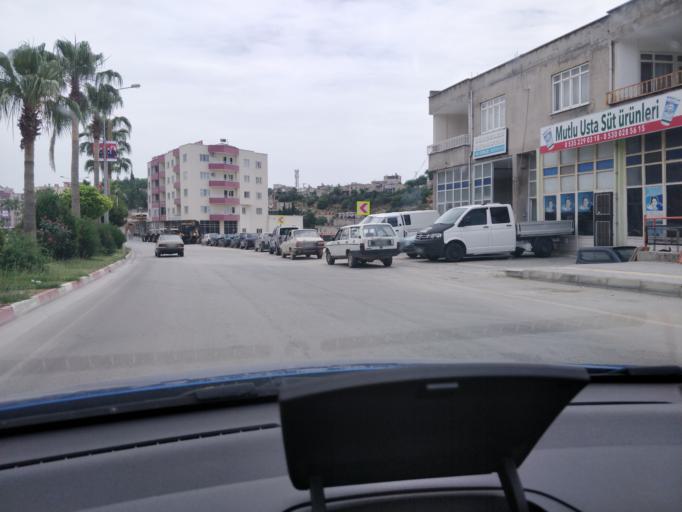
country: TR
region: Mersin
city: Mut
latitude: 36.6461
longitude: 33.4295
